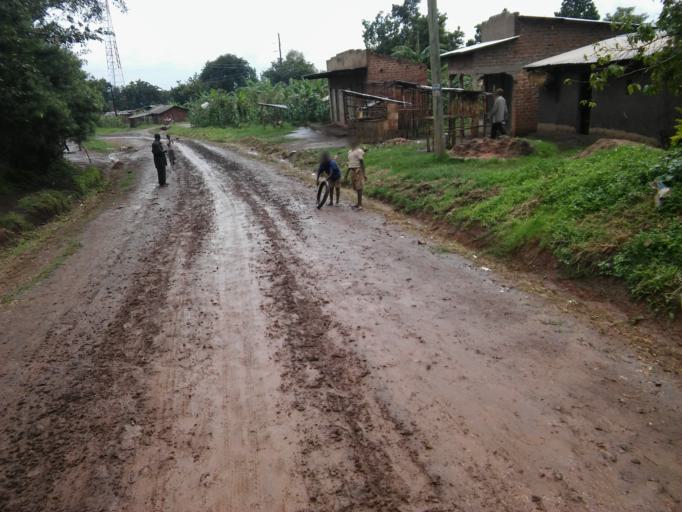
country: UG
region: Eastern Region
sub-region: Mbale District
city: Mbale
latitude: 1.0377
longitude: 34.2055
